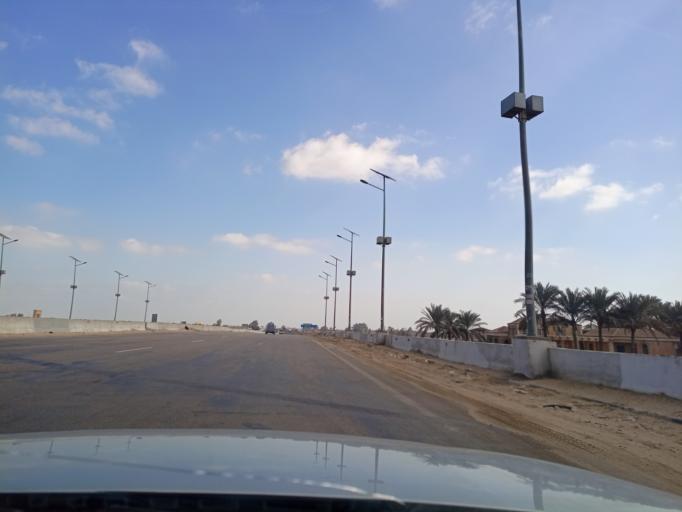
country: EG
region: Muhafazat al Minufiyah
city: Al Bajur
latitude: 30.4048
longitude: 31.0390
